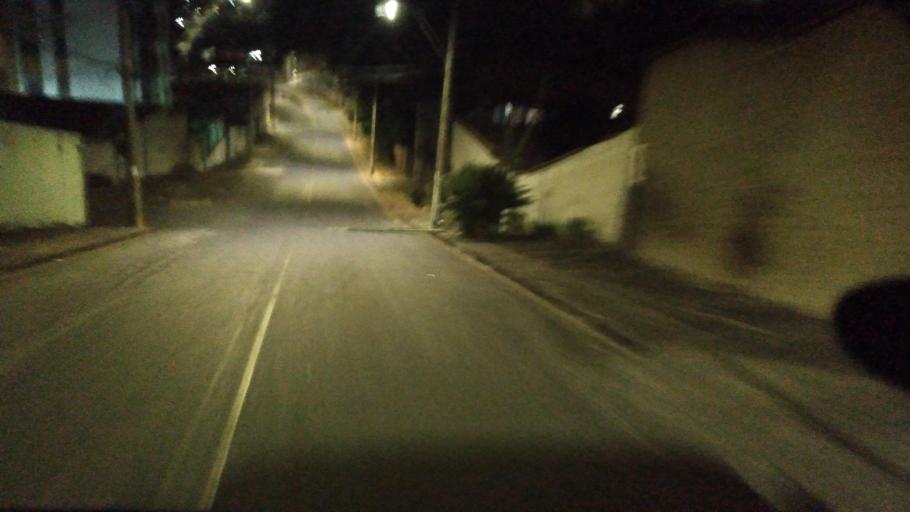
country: BR
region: Minas Gerais
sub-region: Belo Horizonte
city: Belo Horizonte
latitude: -19.8879
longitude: -43.9601
